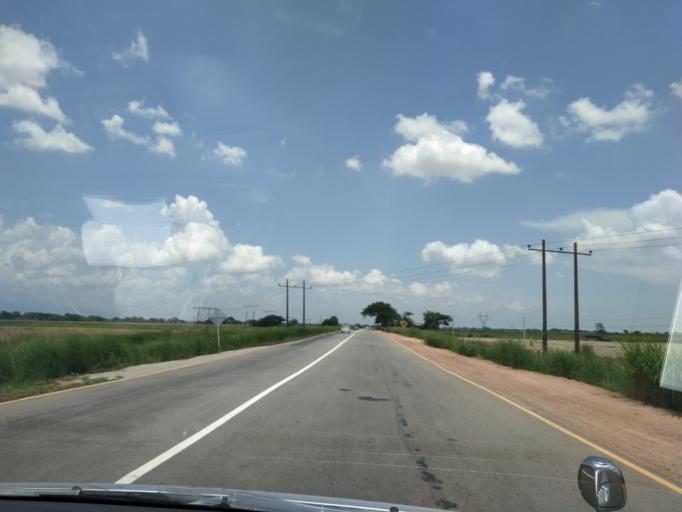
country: MM
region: Mon
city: Kyaikto
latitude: 17.5018
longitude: 96.8061
